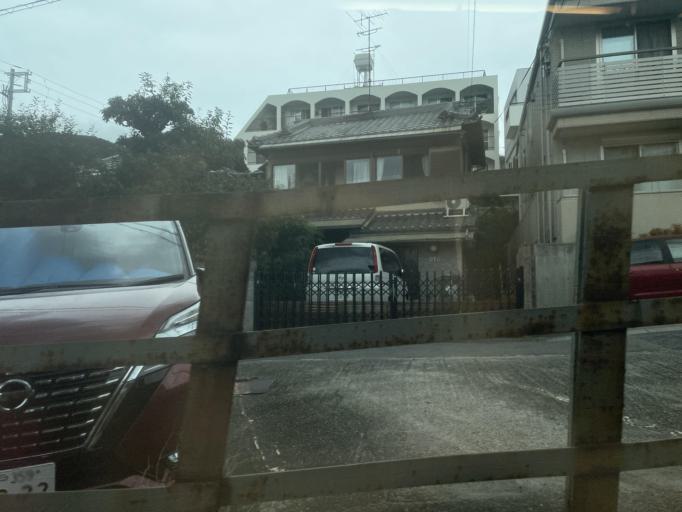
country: JP
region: Hyogo
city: Ashiya
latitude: 34.7296
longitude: 135.2800
